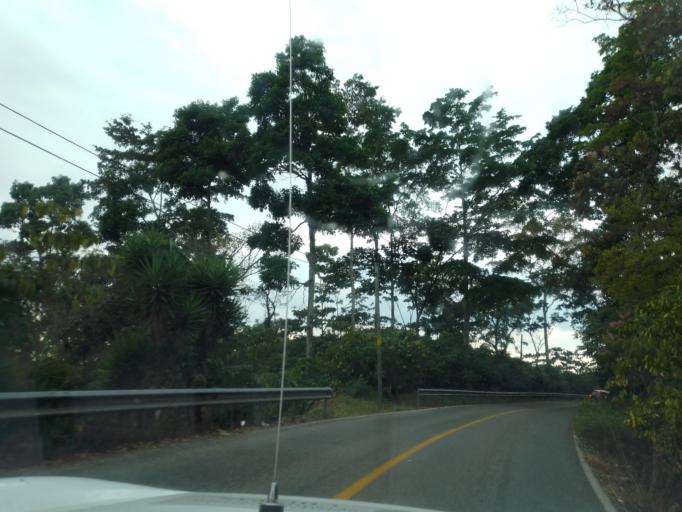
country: MX
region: Chiapas
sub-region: Union Juarez
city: Santo Domingo
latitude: 15.0368
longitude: -92.1272
